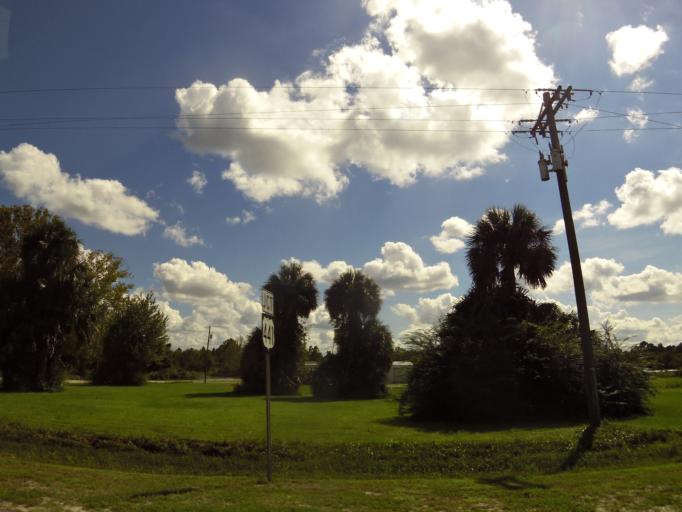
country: US
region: Georgia
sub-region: Clinch County
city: Homerville
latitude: 30.6850
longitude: -82.5638
